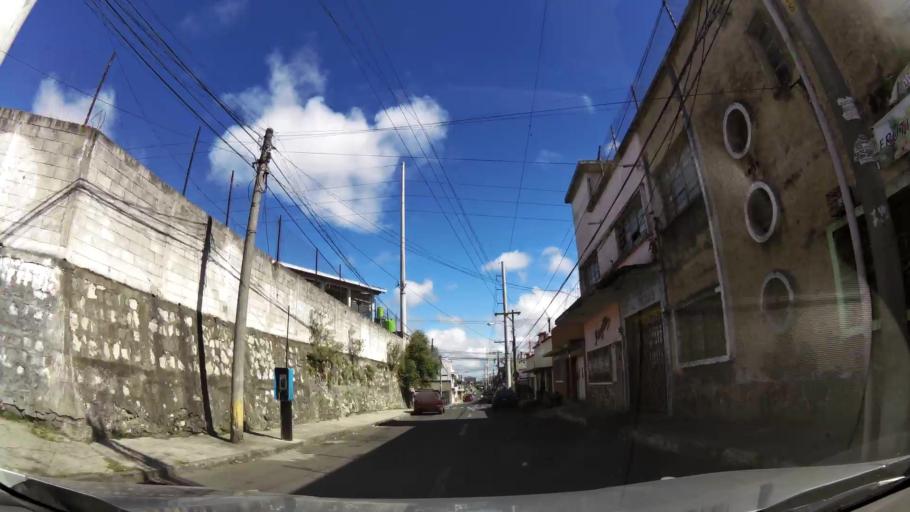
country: GT
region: Guatemala
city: Guatemala City
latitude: 14.6087
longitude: -90.5299
